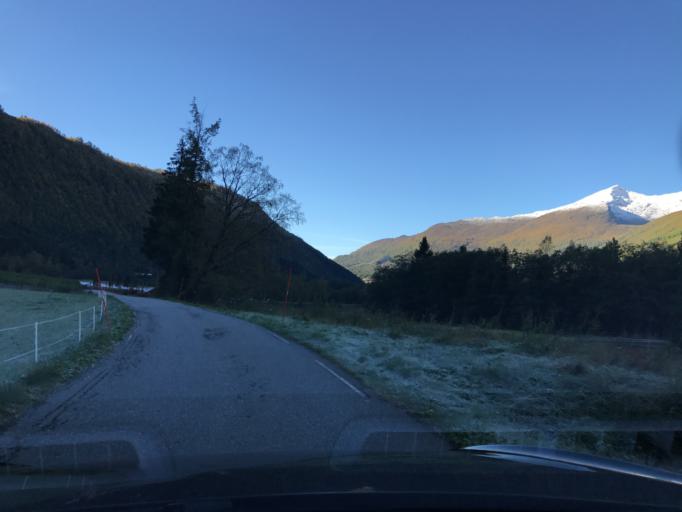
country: NO
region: More og Romsdal
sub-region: Norddal
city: Valldal
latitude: 62.3211
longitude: 7.3262
